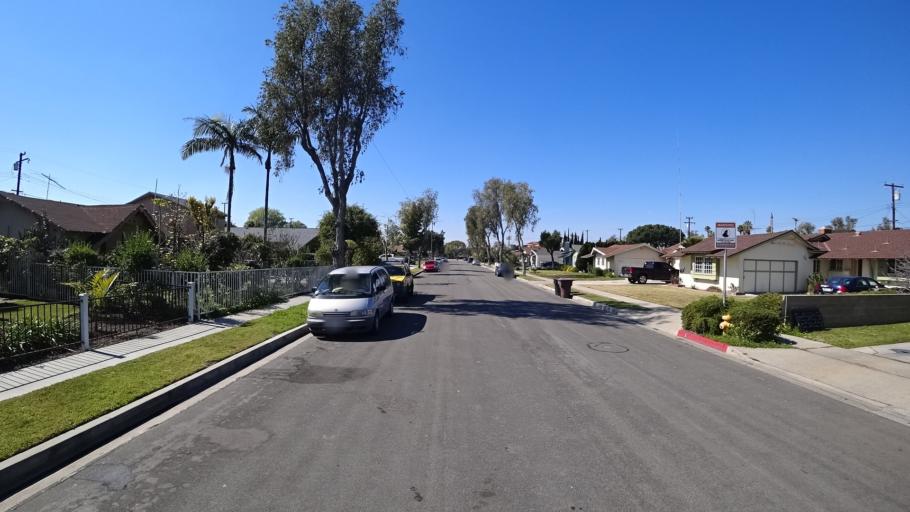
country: US
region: California
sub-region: Orange County
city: Anaheim
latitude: 33.8130
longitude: -117.9350
